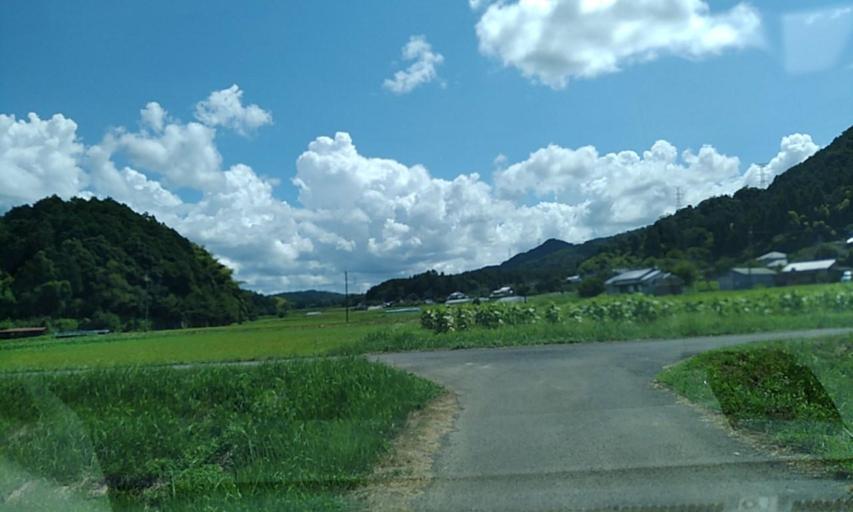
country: JP
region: Kyoto
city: Ayabe
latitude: 35.3464
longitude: 135.2227
